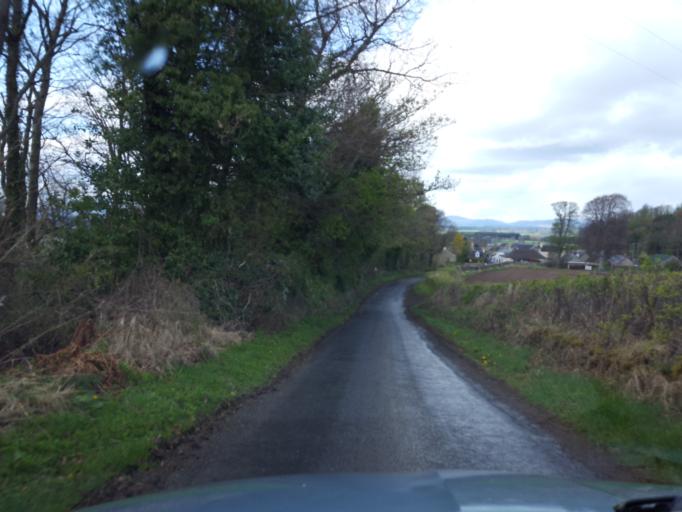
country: GB
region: Scotland
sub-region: Perth and Kinross
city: Methven
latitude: 56.3067
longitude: -3.5779
